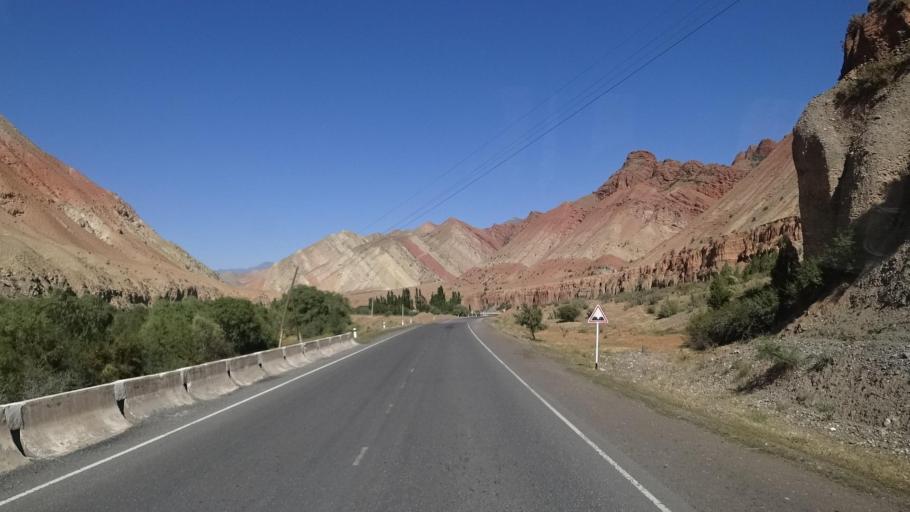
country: KG
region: Osh
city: Gul'cha
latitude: 39.9306
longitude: 73.4531
